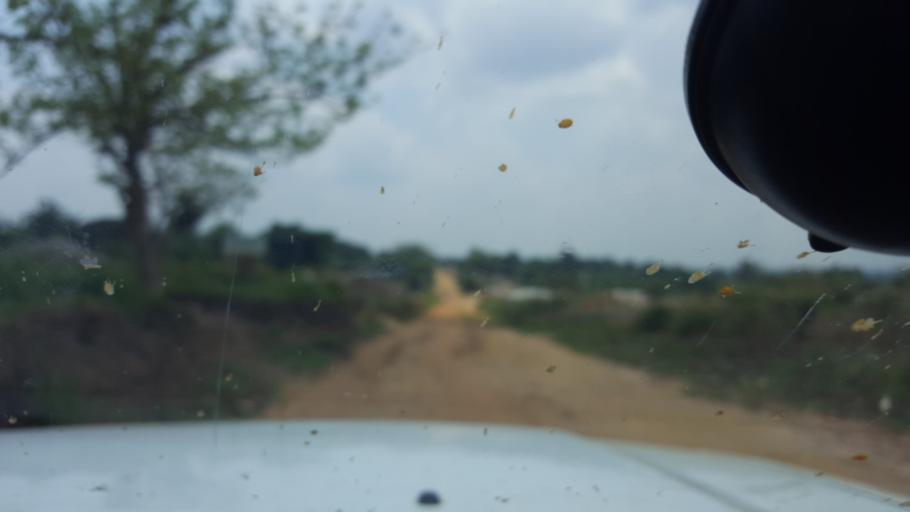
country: CD
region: Bandundu
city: Mushie
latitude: -3.7464
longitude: 16.6501
